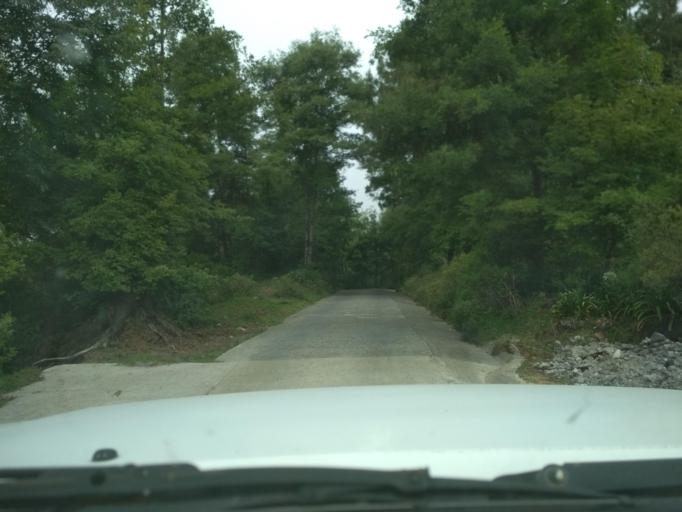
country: MX
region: Veracruz
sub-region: La Perla
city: Chilapa
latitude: 18.9747
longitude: -97.1973
